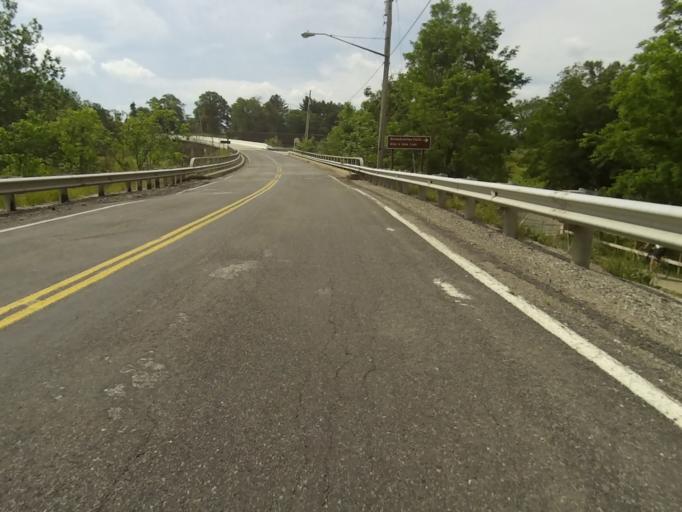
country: US
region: Ohio
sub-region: Summit County
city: Boston Heights
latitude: 41.2768
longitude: -81.5380
